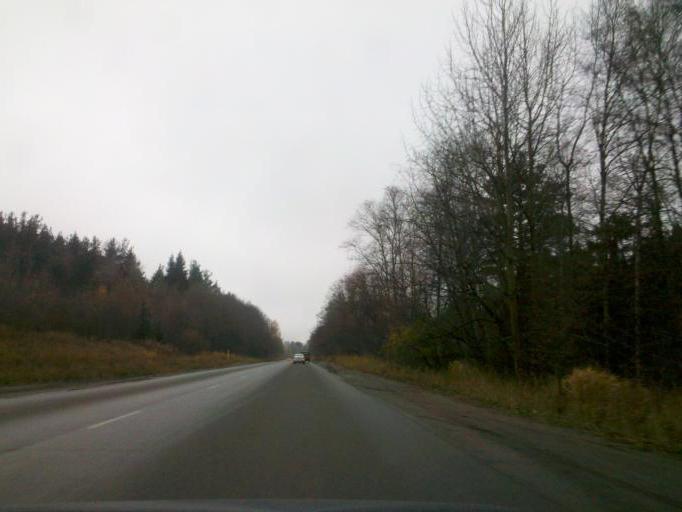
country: RU
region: Republic of Karelia
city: Petrozavodsk
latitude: 61.8204
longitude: 34.2523
